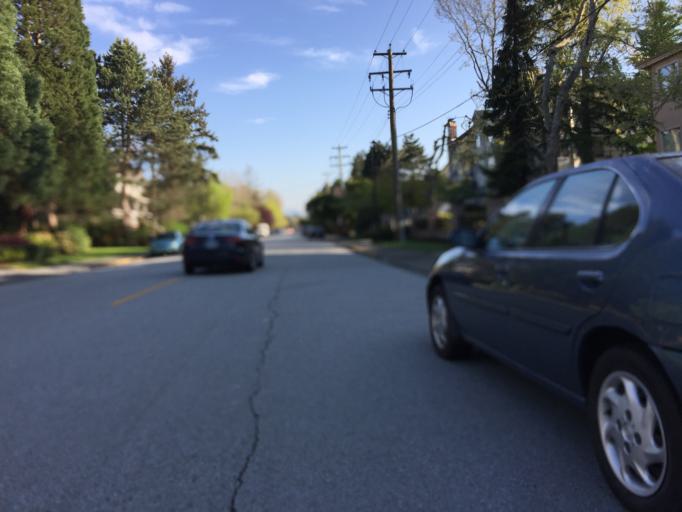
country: CA
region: British Columbia
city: Richmond
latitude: 49.1572
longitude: -123.1435
